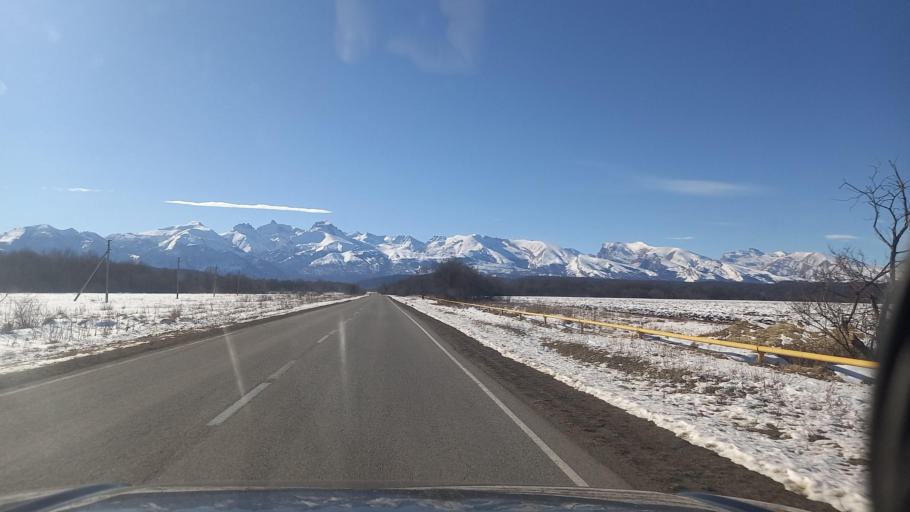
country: RU
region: North Ossetia
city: Chikola
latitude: 43.1687
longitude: 43.8632
